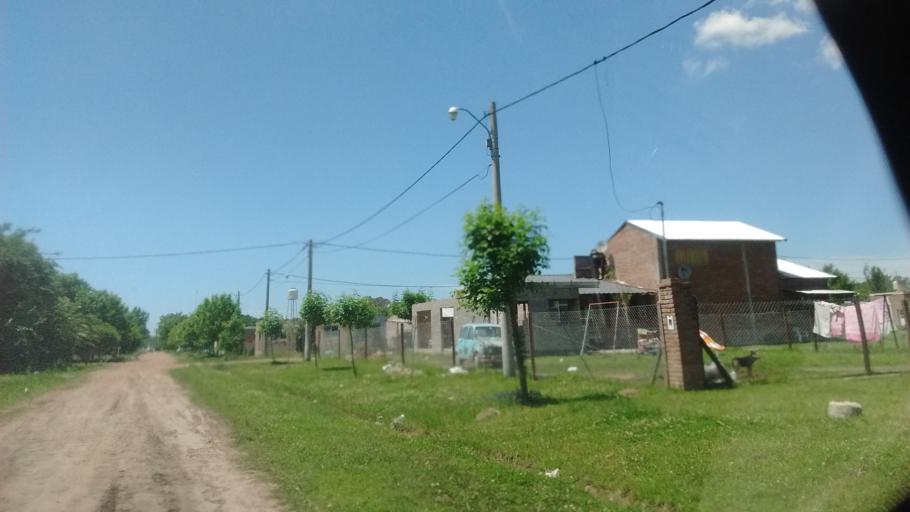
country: AR
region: Santa Fe
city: Funes
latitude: -32.8509
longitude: -60.7976
